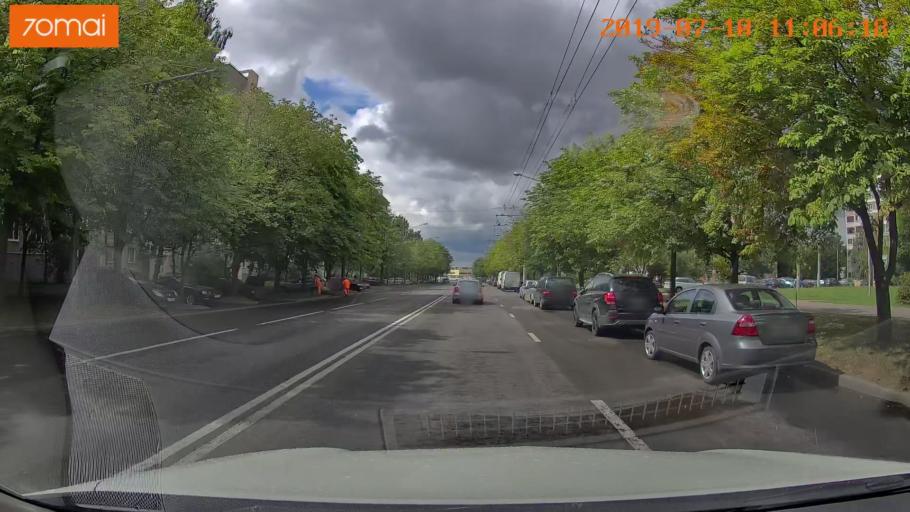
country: BY
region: Minsk
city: Syenitsa
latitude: 53.8503
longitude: 27.5460
